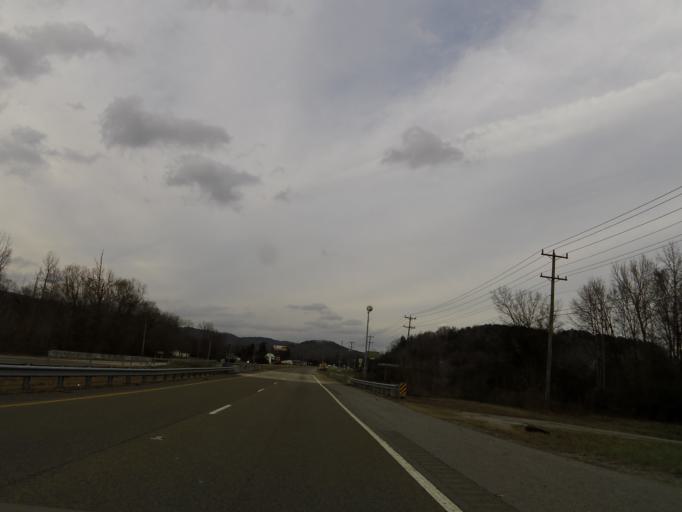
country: US
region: Tennessee
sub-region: Hamilton County
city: Sale Creek
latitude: 35.3368
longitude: -85.1293
